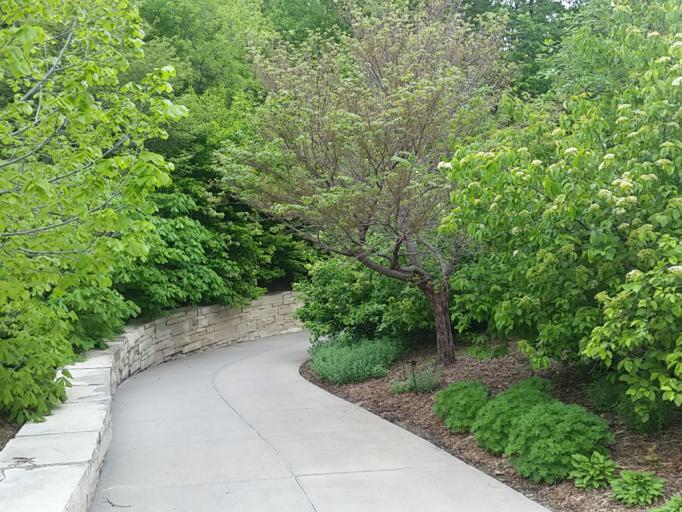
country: US
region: Nebraska
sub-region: Douglas County
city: Omaha
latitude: 41.2352
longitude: -95.9158
